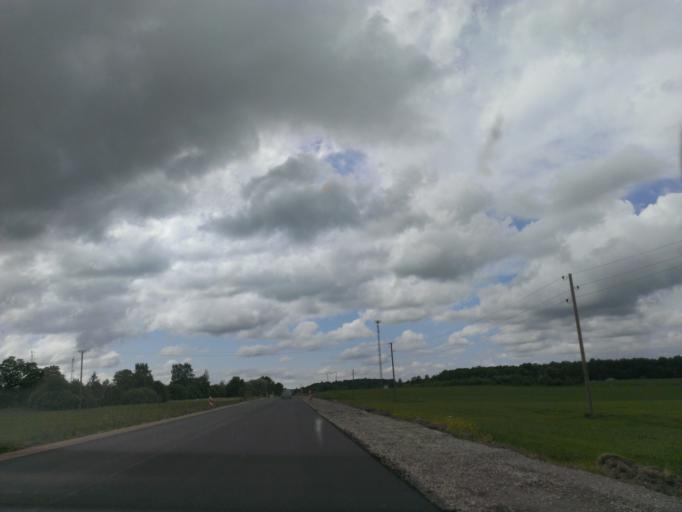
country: LV
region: Durbe
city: Liegi
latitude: 56.5905
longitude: 21.4075
